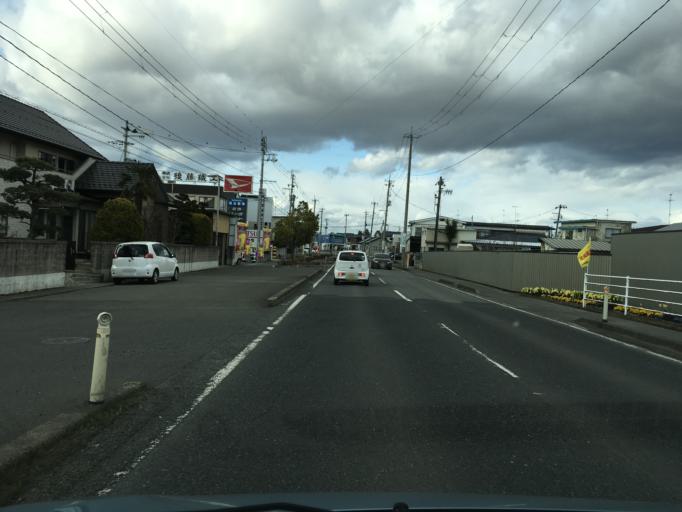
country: JP
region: Miyagi
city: Wakuya
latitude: 38.6767
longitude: 141.1937
